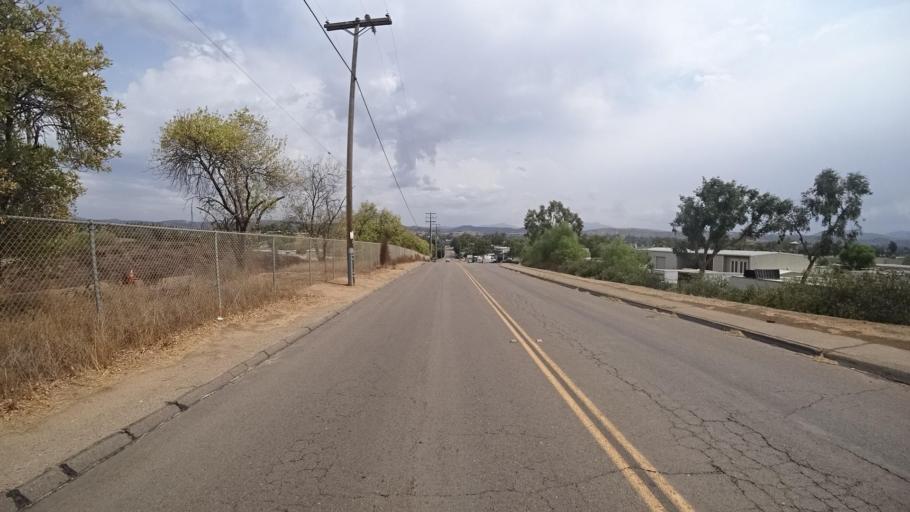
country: US
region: California
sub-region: San Diego County
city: Ramona
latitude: 33.0476
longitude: -116.8763
